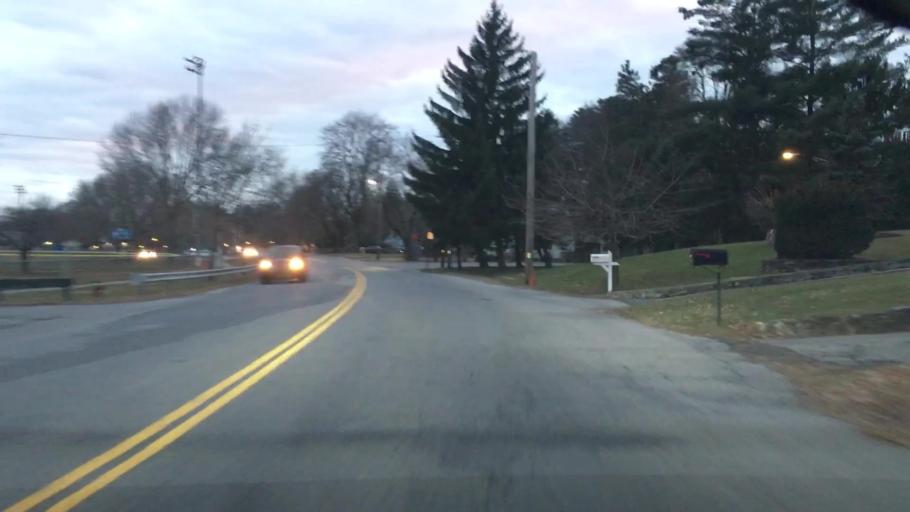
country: US
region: New York
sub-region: Dutchess County
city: Spackenkill
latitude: 41.6764
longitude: -73.9126
